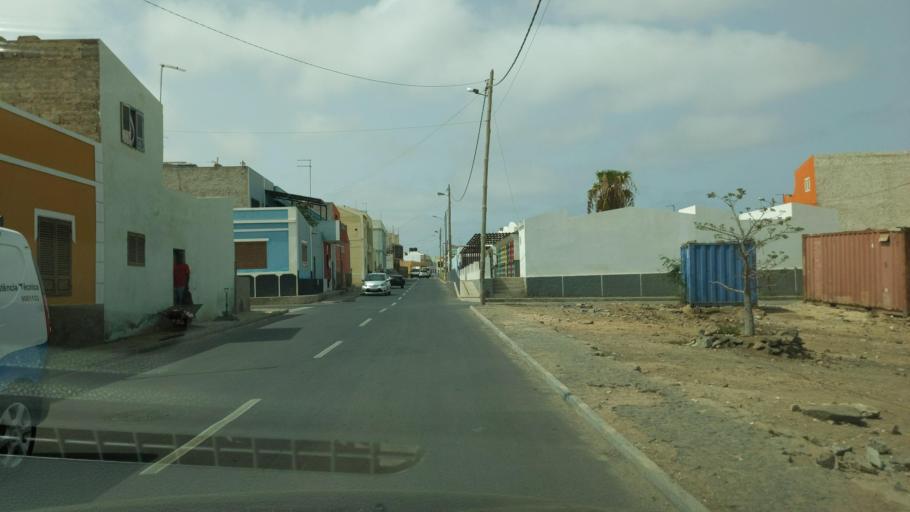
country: CV
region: Sal
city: Espargos
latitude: 16.7568
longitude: -22.9472
